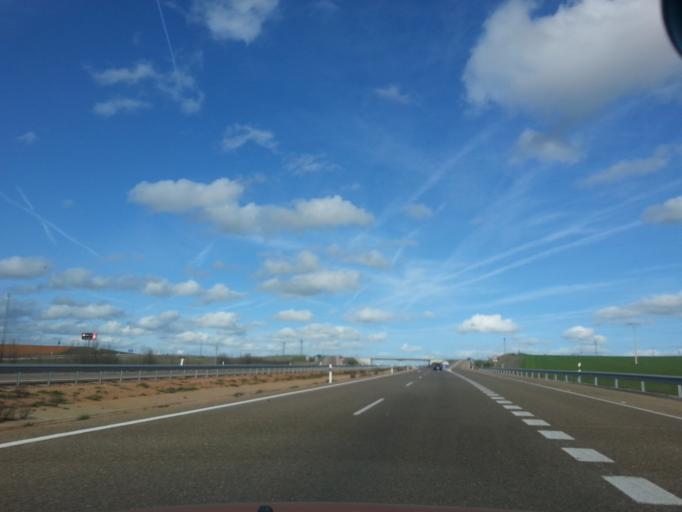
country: ES
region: Castille and Leon
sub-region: Provincia de Salamanca
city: Robliza de Cojos
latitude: 40.8732
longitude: -5.9861
